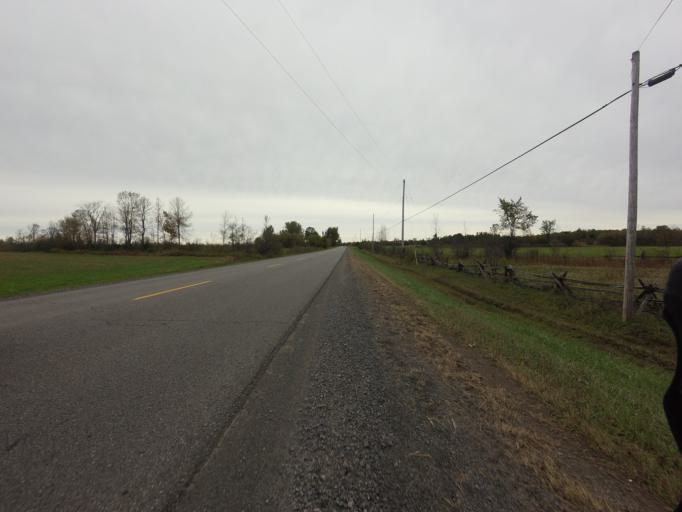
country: CA
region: Ontario
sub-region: Lanark County
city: Smiths Falls
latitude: 44.8576
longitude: -75.8106
